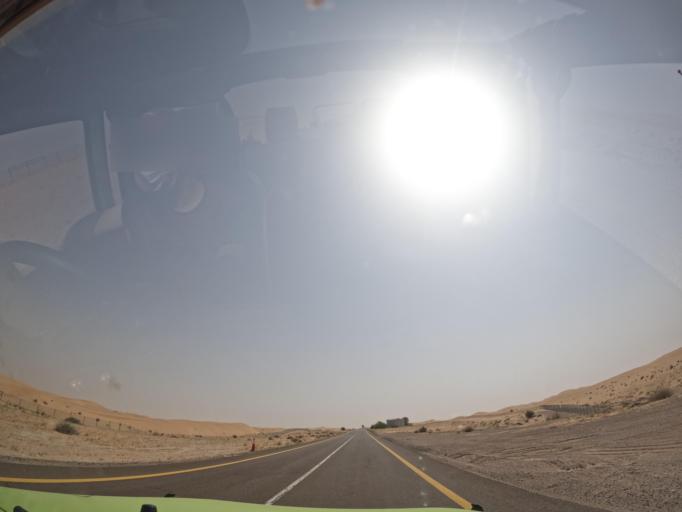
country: OM
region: Al Buraimi
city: Al Buraymi
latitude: 24.6420
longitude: 55.5079
